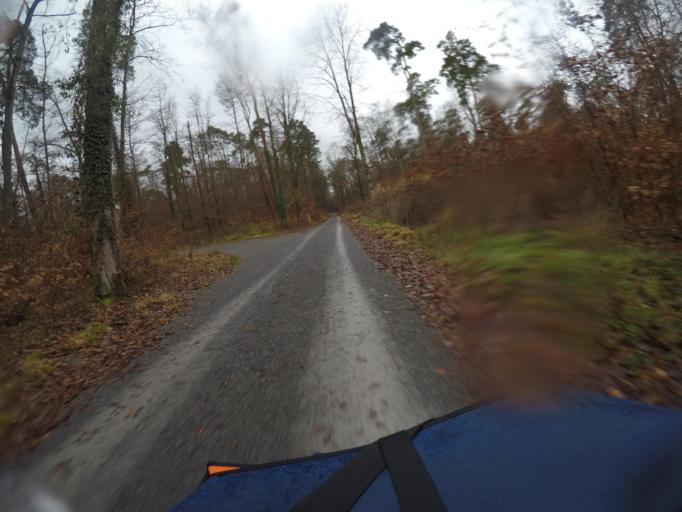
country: DE
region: Baden-Wuerttemberg
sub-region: Karlsruhe Region
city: Graben-Neudorf
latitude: 49.1401
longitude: 8.4571
